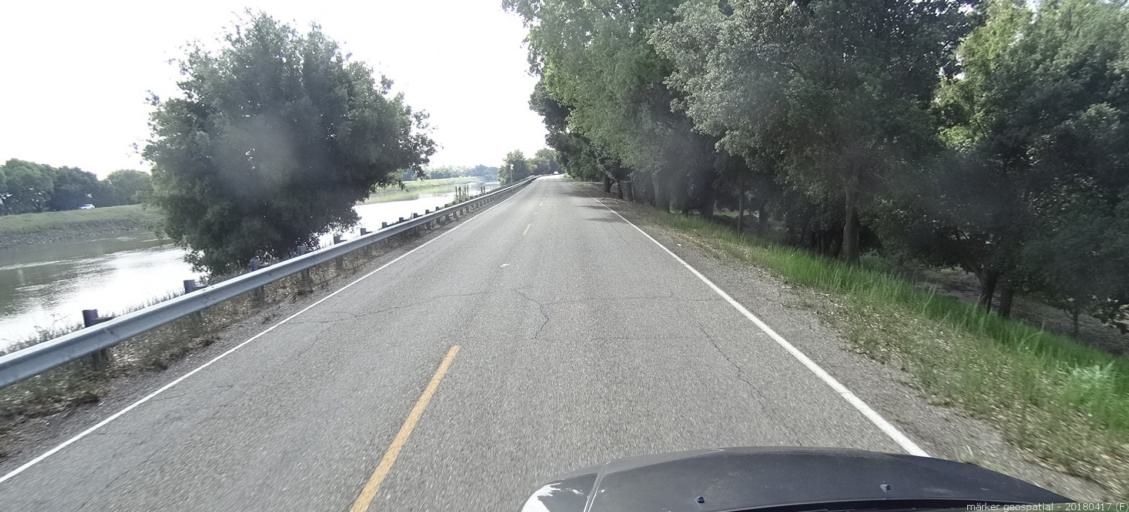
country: US
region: California
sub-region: Sacramento County
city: Walnut Grove
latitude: 38.2633
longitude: -121.5261
